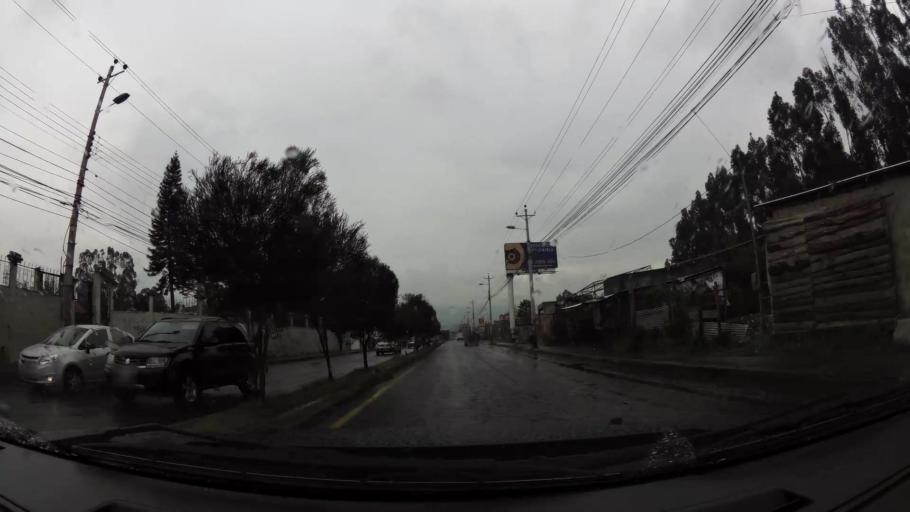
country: EC
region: Pichincha
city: Sangolqui
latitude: -0.3092
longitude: -78.4448
